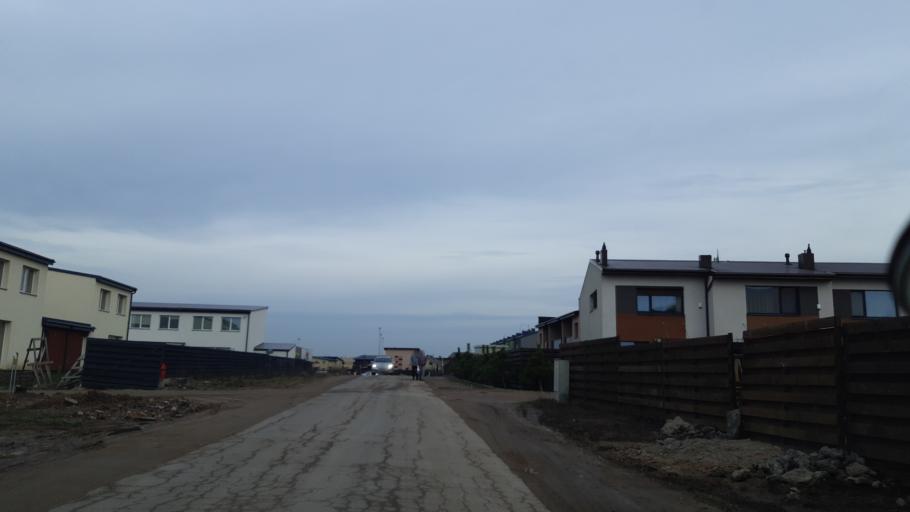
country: LT
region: Kauno apskritis
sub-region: Kauno rajonas
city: Akademija (Kaunas)
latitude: 54.9447
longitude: 23.8255
